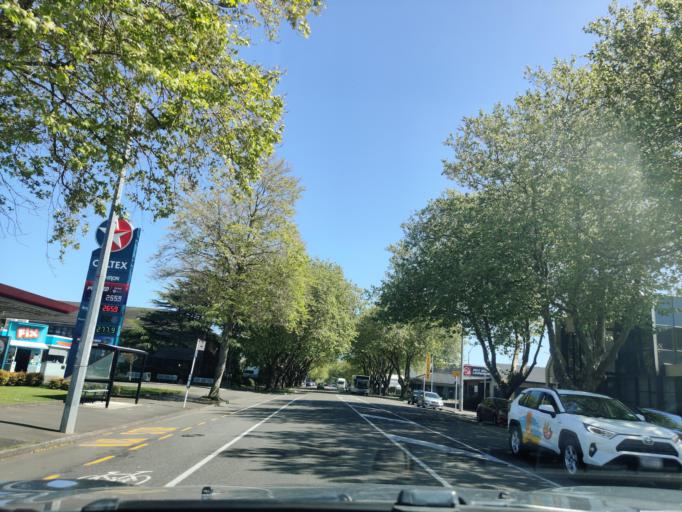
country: NZ
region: Manawatu-Wanganui
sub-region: Wanganui District
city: Wanganui
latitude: -39.9296
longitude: 175.0465
